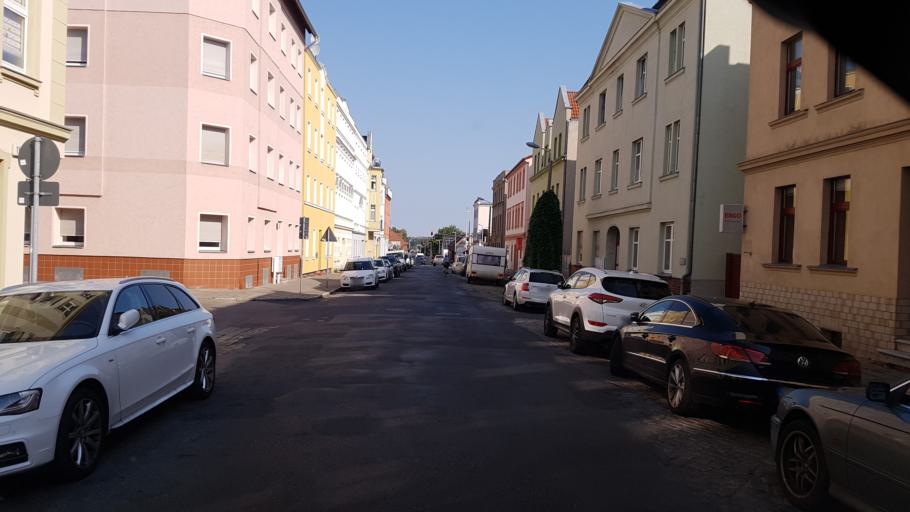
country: DE
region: Brandenburg
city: Cottbus
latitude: 51.7531
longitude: 14.3037
